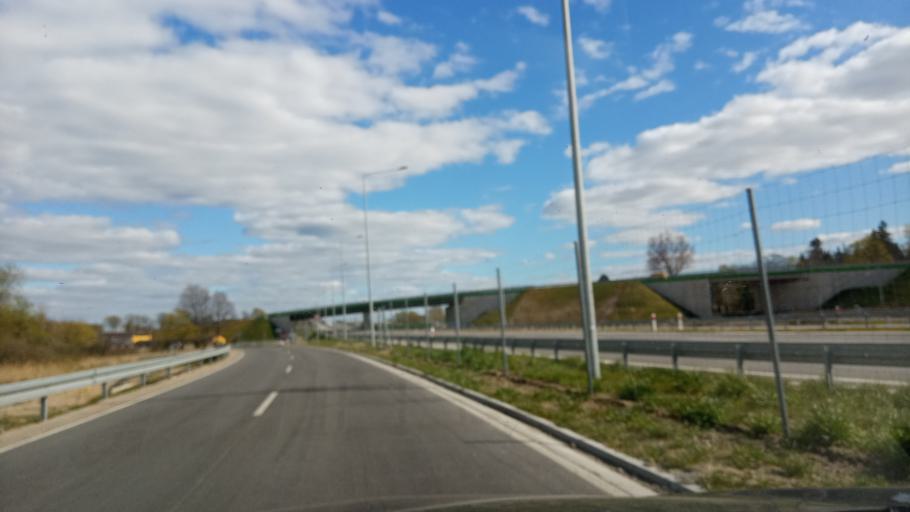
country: PL
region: West Pomeranian Voivodeship
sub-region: Powiat szczecinecki
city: Szczecinek
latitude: 53.7145
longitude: 16.7102
